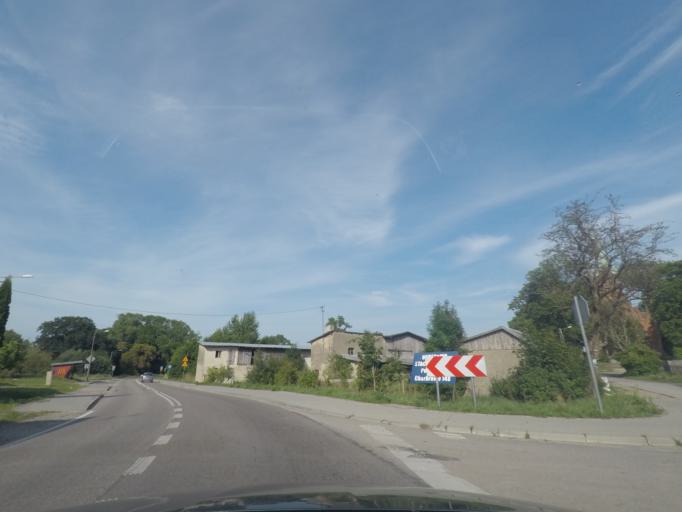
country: PL
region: Pomeranian Voivodeship
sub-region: Powiat leborski
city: Leba
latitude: 54.6428
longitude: 17.5420
